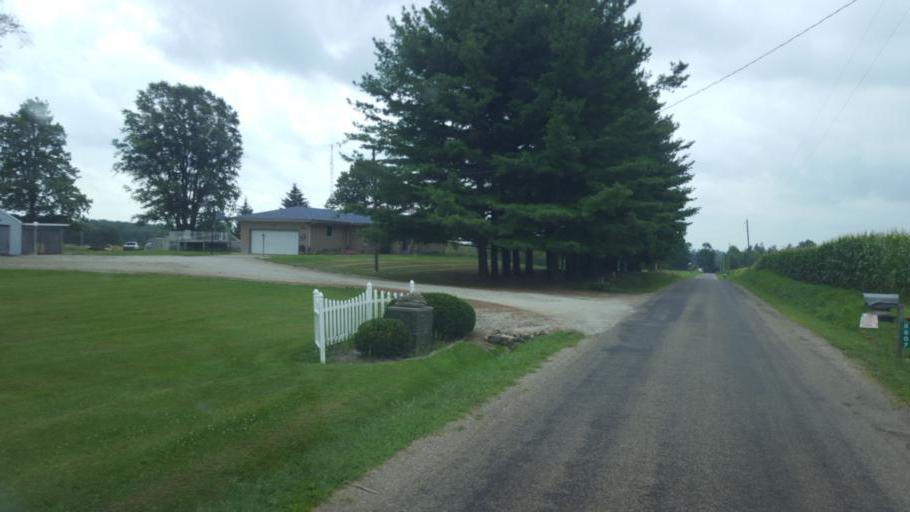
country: US
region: Ohio
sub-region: Richland County
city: Lexington
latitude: 40.6745
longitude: -82.6362
